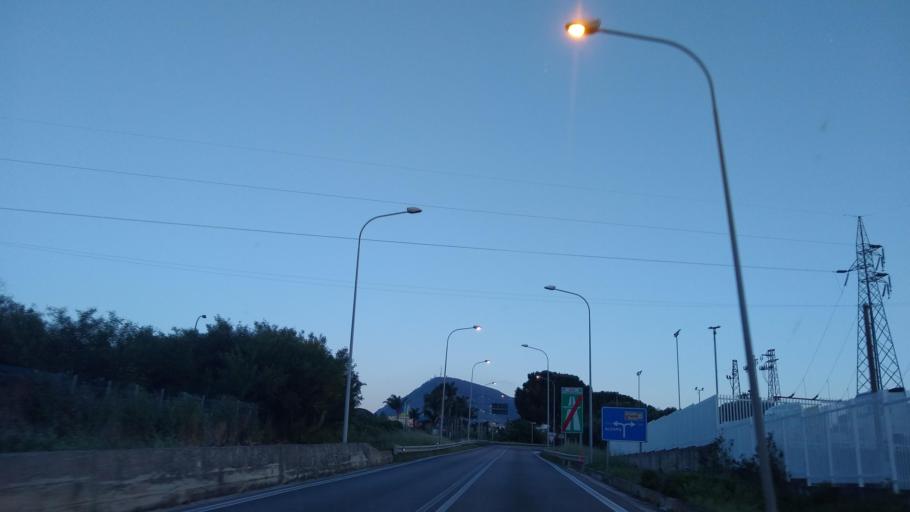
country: IT
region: Sicily
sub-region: Trapani
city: Alcamo
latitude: 38.0019
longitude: 12.9575
